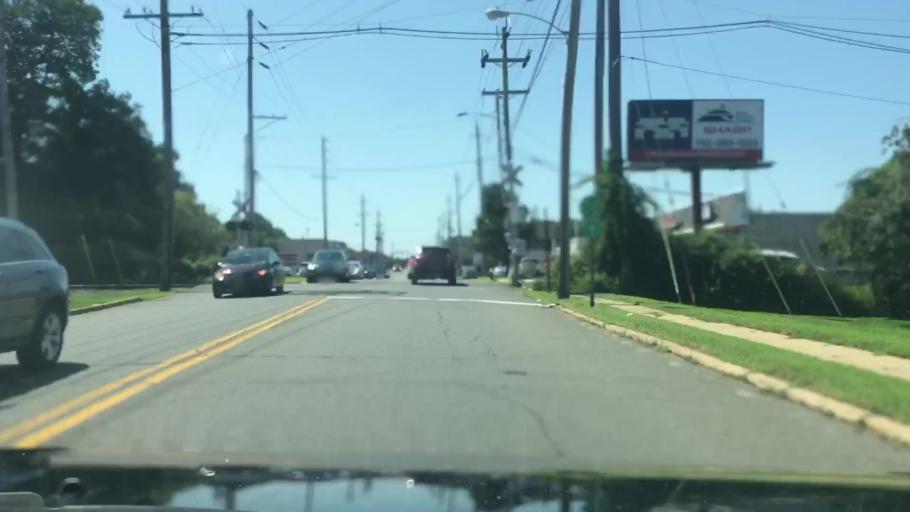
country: US
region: New Jersey
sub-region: Monmouth County
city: Red Bank
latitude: 40.3377
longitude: -74.0710
